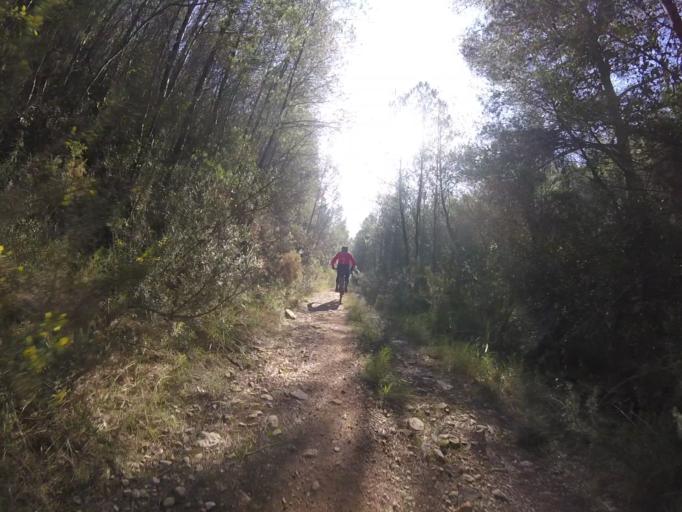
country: ES
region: Valencia
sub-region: Provincia de Castello
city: Santa Magdalena de Pulpis
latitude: 40.3107
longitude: 0.3335
